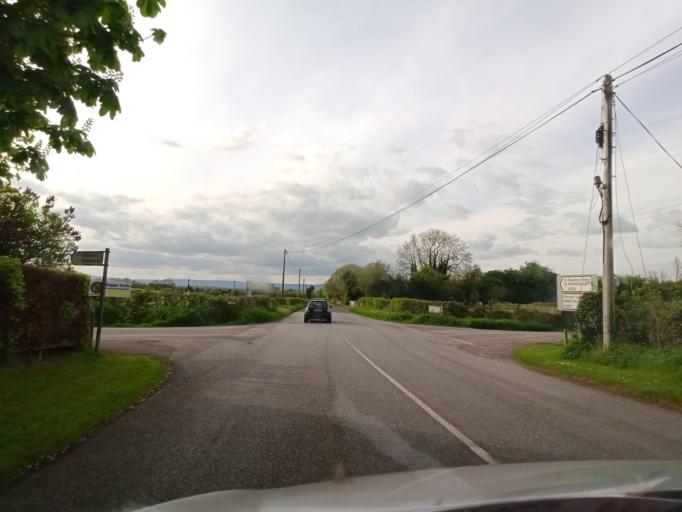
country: IE
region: Leinster
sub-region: Laois
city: Abbeyleix
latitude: 52.9407
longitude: -7.3809
